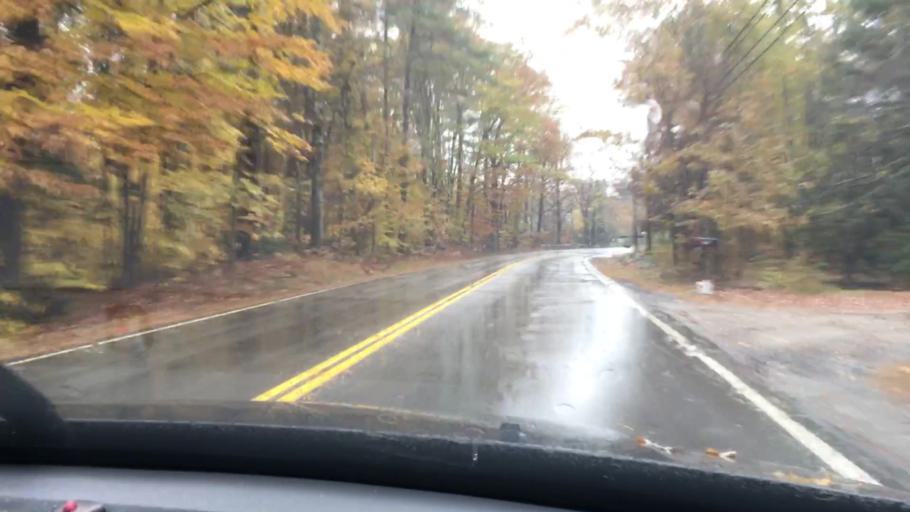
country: US
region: New Hampshire
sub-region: Belknap County
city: Meredith
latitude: 43.7057
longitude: -71.5217
